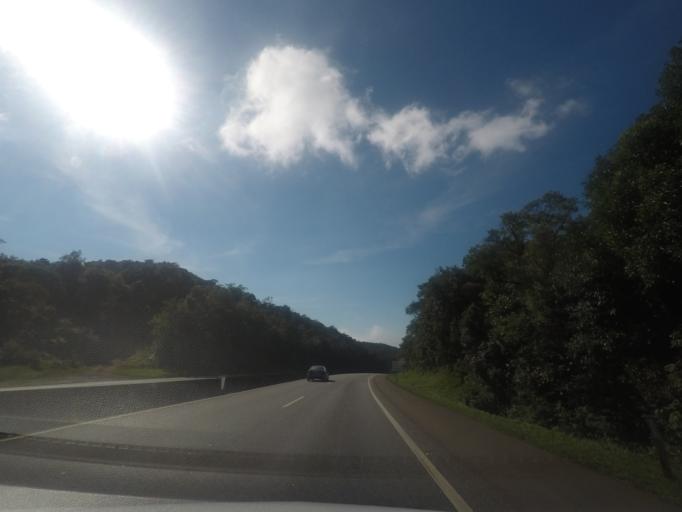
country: BR
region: Parana
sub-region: Piraquara
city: Piraquara
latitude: -25.5915
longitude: -48.9223
